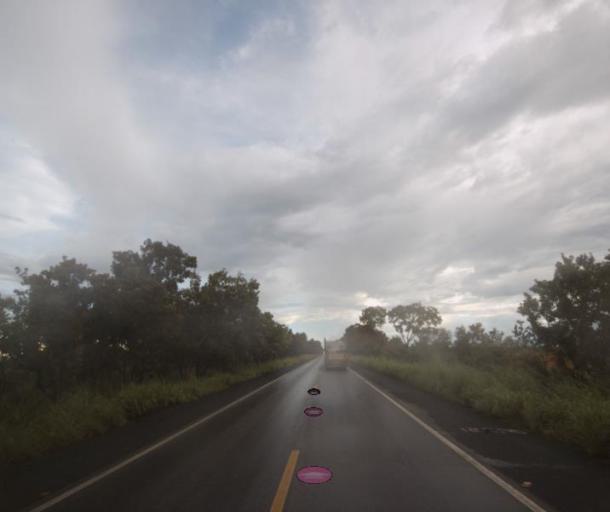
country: BR
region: Goias
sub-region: Porangatu
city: Porangatu
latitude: -13.8525
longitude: -49.0484
